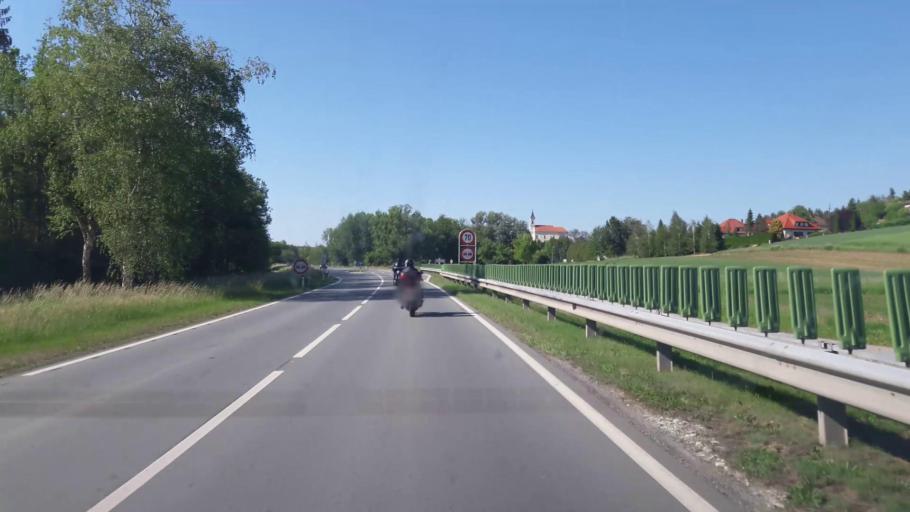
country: AT
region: Burgenland
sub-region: Politischer Bezirk Oberwart
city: Litzelsdorf
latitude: 47.2013
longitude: 16.1607
